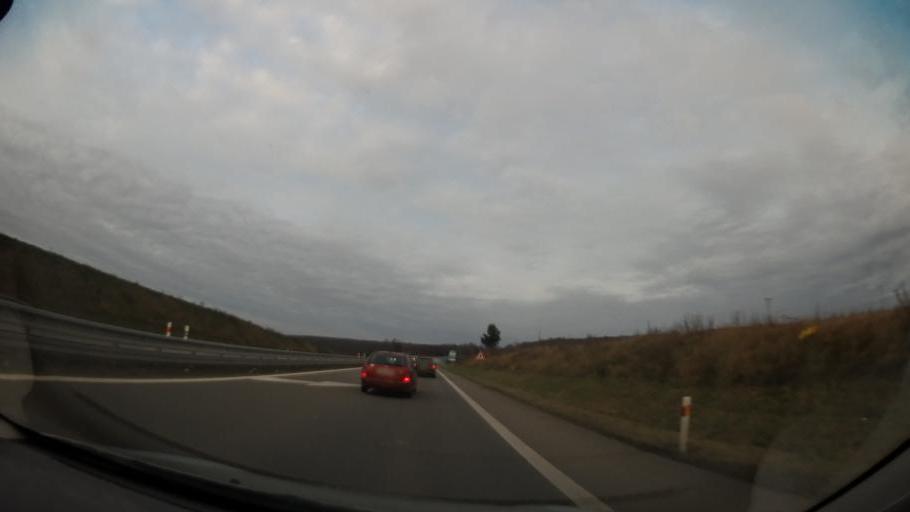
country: CZ
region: South Moravian
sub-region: Okres Brno-Venkov
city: Rosice
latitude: 49.1908
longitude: 16.4175
